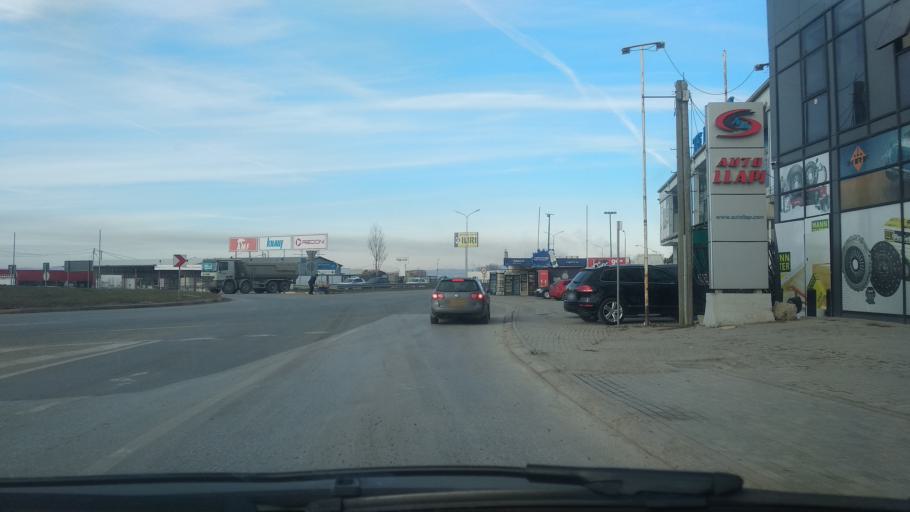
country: XK
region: Pristina
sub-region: Komuna e Prishtines
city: Pristina
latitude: 42.6582
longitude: 21.1369
